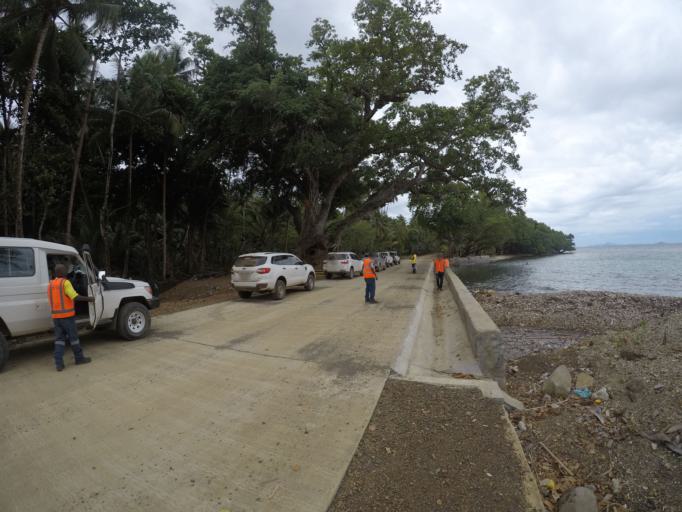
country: PG
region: Milne Bay
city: Alotau
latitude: -10.2841
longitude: 150.7728
